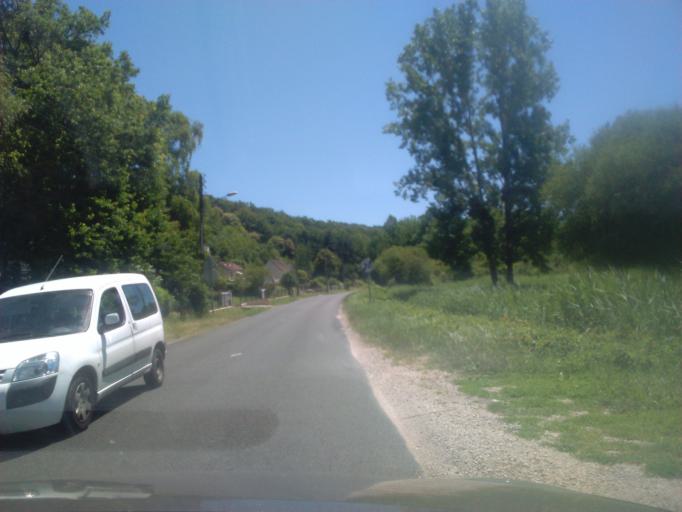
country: FR
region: Centre
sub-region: Departement du Loir-et-Cher
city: Saint-Sulpice-de-Pommeray
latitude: 47.5738
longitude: 1.2186
